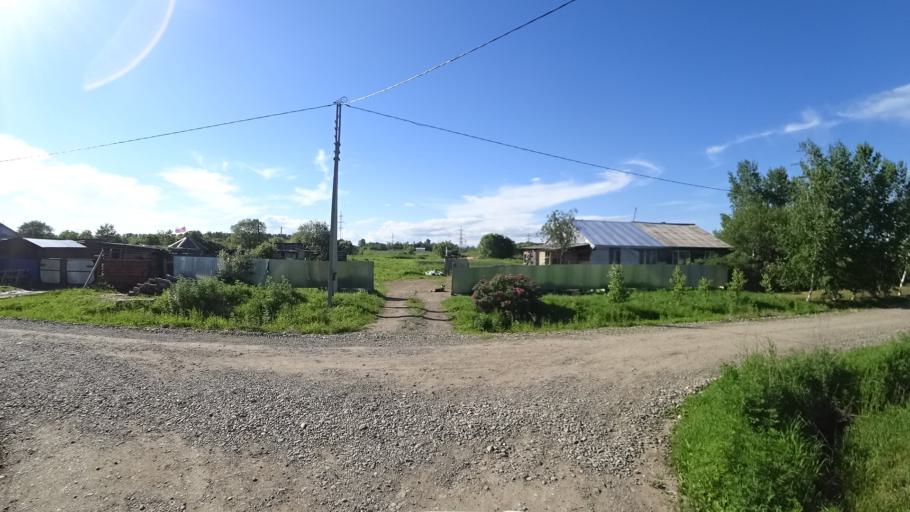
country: RU
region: Khabarovsk Krai
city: Khor
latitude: 47.8947
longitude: 134.9933
